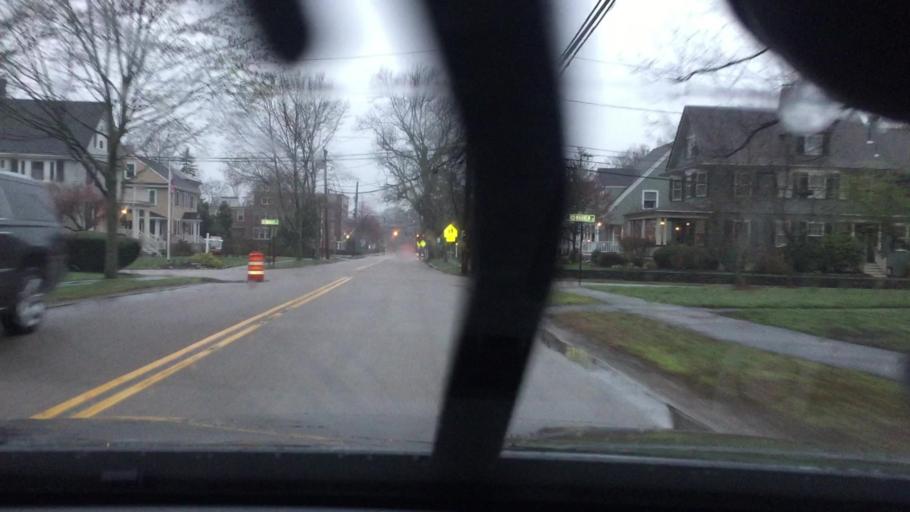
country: US
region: Massachusetts
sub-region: Norfolk County
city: Needham
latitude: 42.2829
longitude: -71.2325
